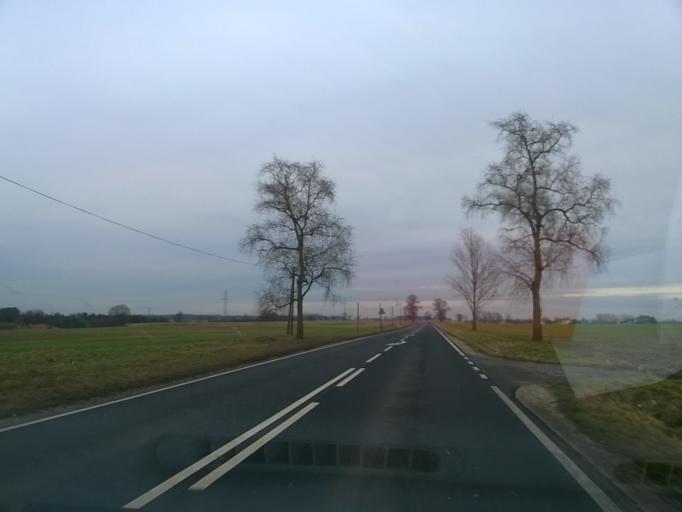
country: PL
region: Kujawsko-Pomorskie
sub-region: Powiat nakielski
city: Naklo nad Notecia
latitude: 53.0990
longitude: 17.6363
